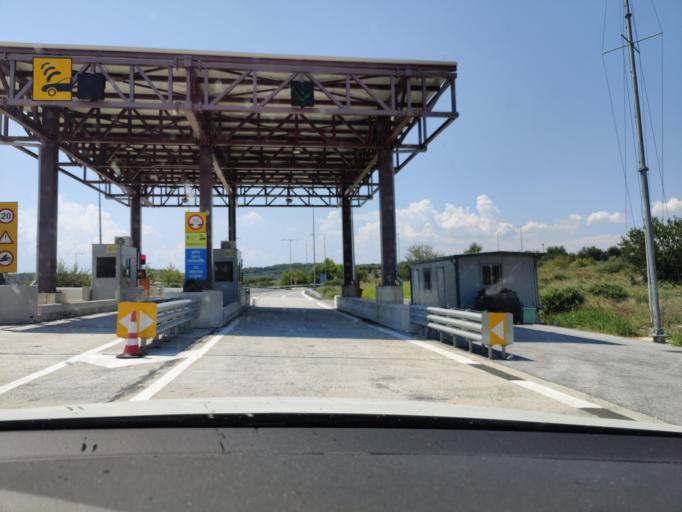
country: GR
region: East Macedonia and Thrace
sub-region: Nomos Kavalas
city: Paralia Ofryniou
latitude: 40.7829
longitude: 23.9578
